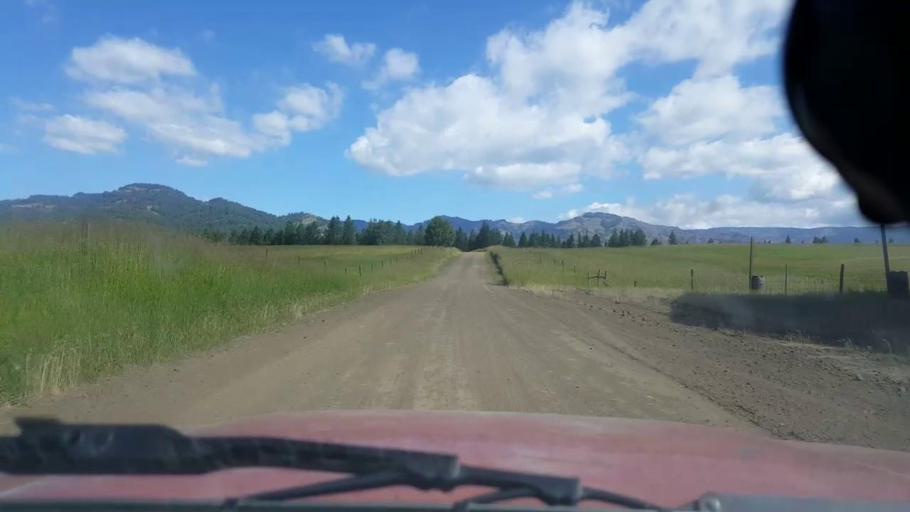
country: US
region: Washington
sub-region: Asotin County
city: Asotin
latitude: 46.0338
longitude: -117.4072
